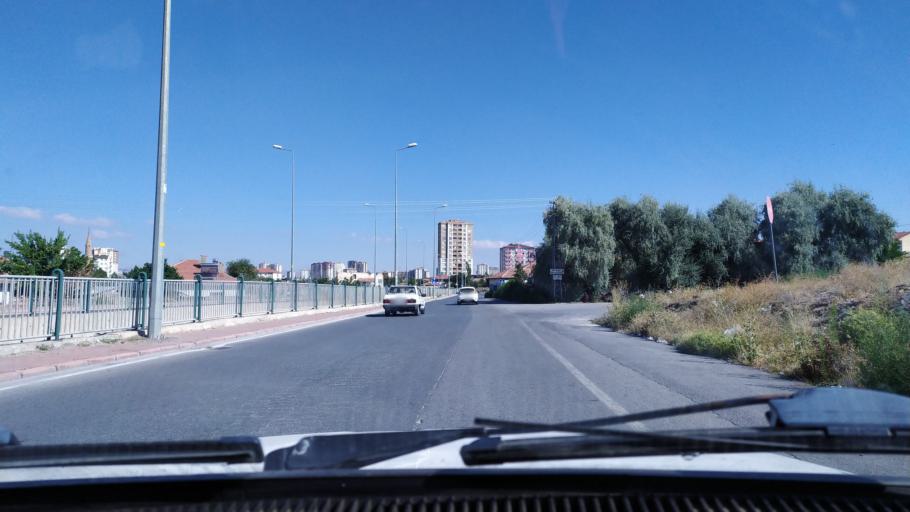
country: TR
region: Kayseri
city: Talas
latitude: 38.7249
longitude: 35.5505
